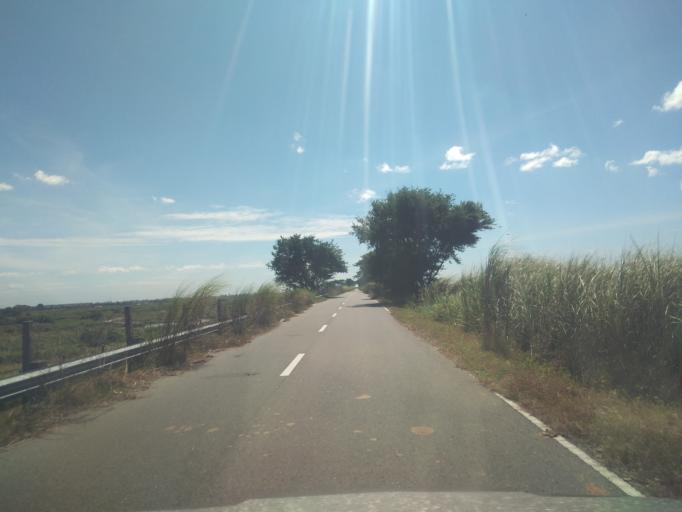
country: PH
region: Central Luzon
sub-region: Province of Pampanga
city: San Basilio
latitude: 15.0386
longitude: 120.5952
